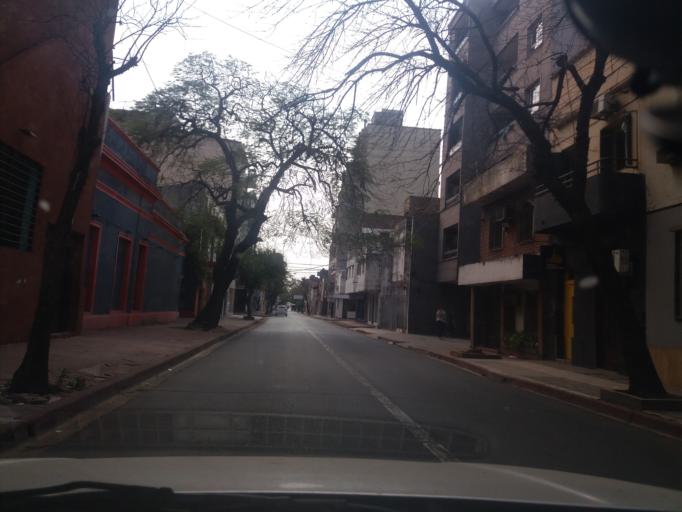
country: AR
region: Corrientes
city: Corrientes
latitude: -27.4725
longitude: -58.8386
